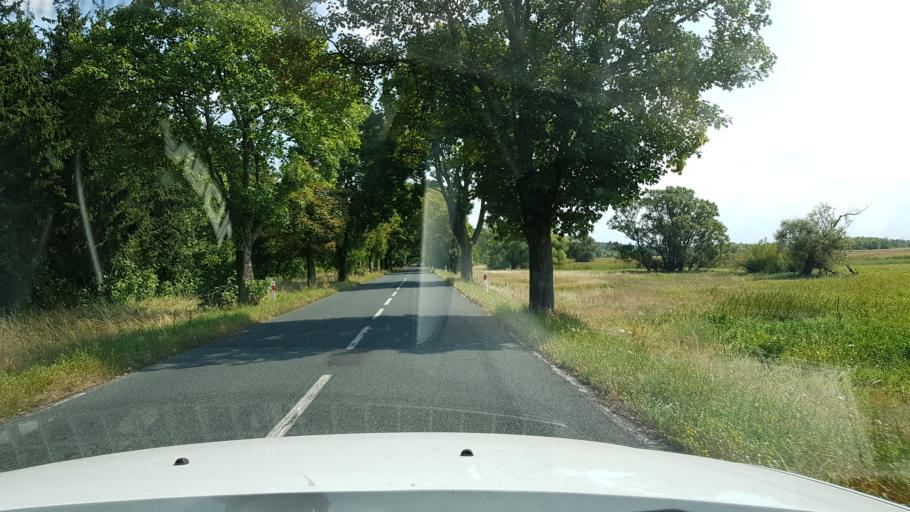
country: PL
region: West Pomeranian Voivodeship
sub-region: Powiat gryfinski
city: Cedynia
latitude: 52.8310
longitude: 14.2134
